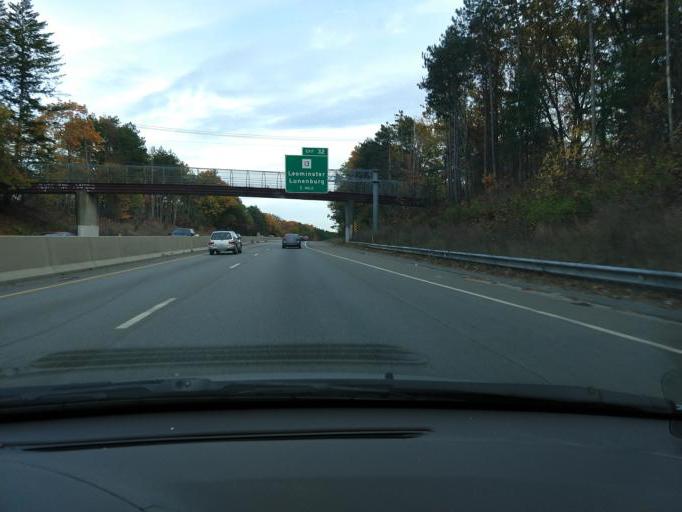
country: US
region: Massachusetts
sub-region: Worcester County
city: Leominster
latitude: 42.5454
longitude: -71.7582
